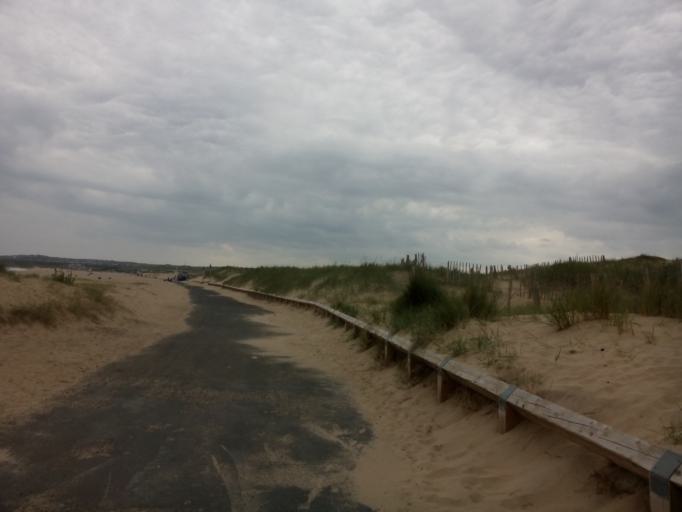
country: GB
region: England
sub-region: South Tyneside
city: South Shields
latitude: 55.0033
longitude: -1.4153
